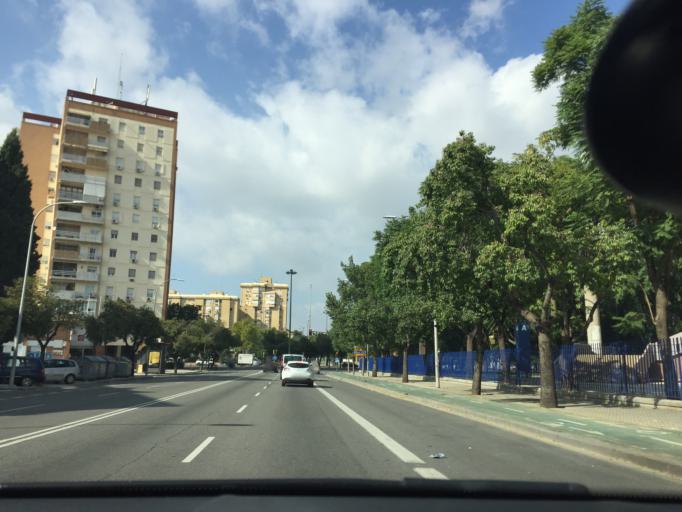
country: ES
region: Andalusia
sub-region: Provincia de Sevilla
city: Sevilla
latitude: 37.3960
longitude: -5.9650
